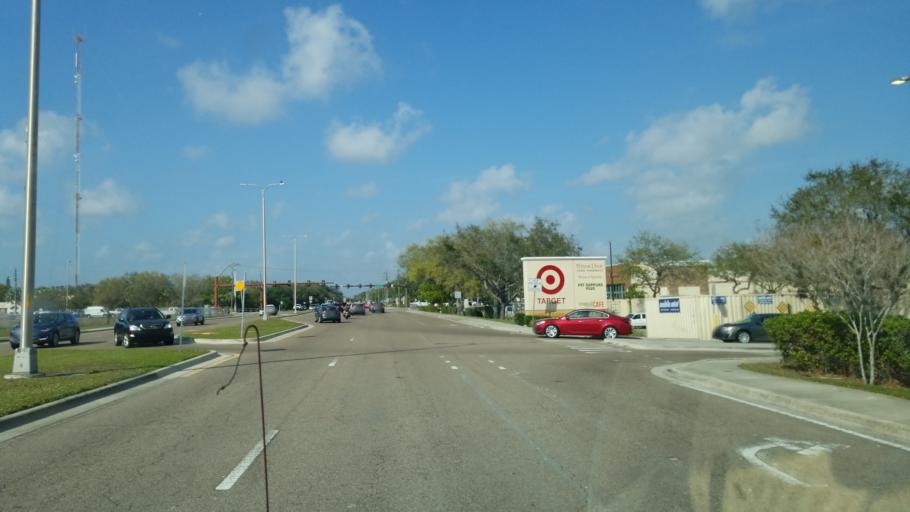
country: US
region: Florida
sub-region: Sarasota County
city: Fruitville
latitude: 27.3361
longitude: -82.4637
